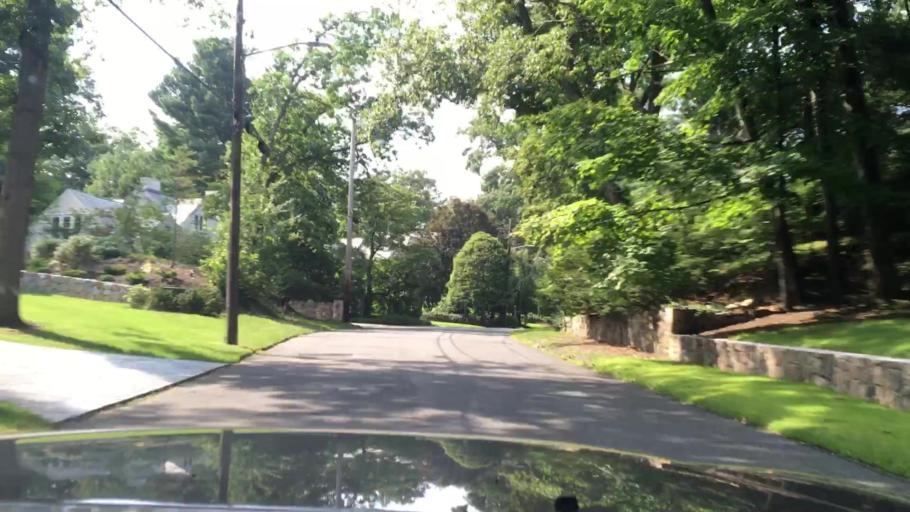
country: US
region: Massachusetts
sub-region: Norfolk County
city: Wellesley
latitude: 42.3126
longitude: -71.2803
